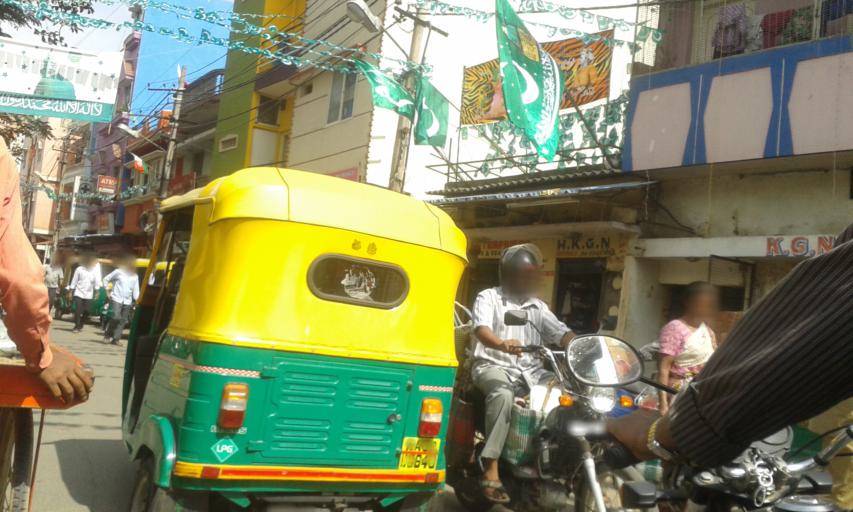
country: IN
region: Karnataka
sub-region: Bangalore Urban
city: Bangalore
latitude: 12.9521
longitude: 77.6118
